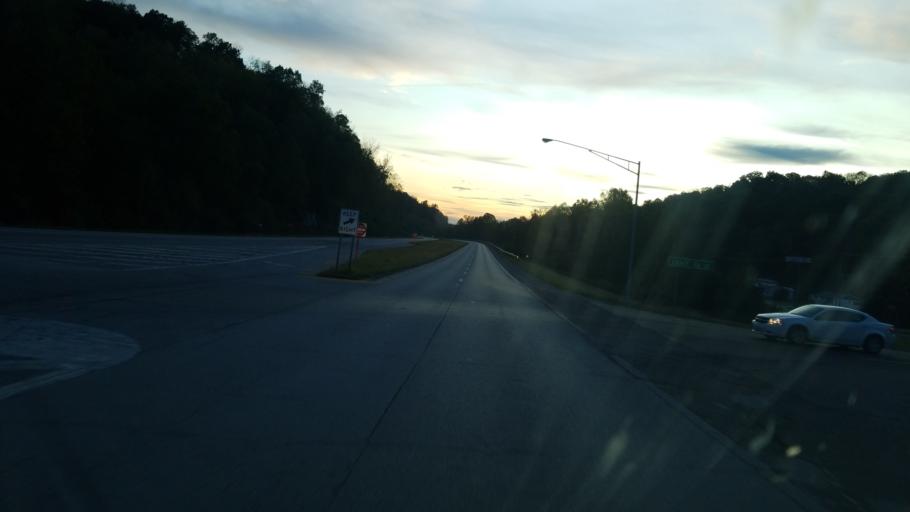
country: US
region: Ohio
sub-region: Meigs County
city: Pomeroy
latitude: 39.0562
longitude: -82.0262
